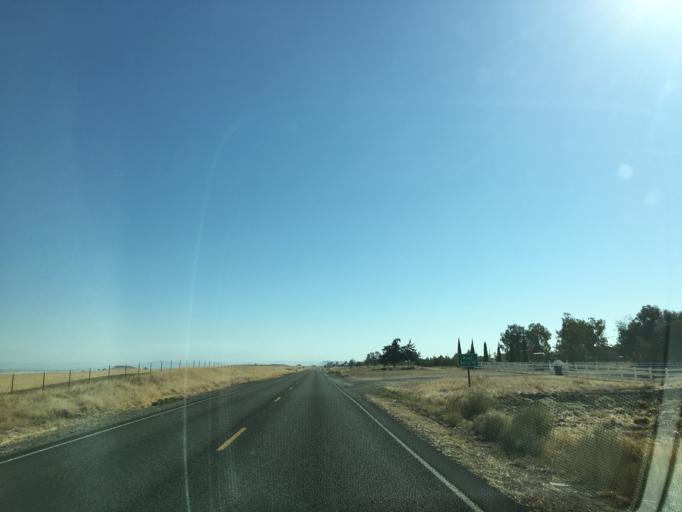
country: US
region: California
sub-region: Madera County
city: Bonadelle Ranchos-Madera Ranchos
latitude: 37.0103
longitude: -119.8882
